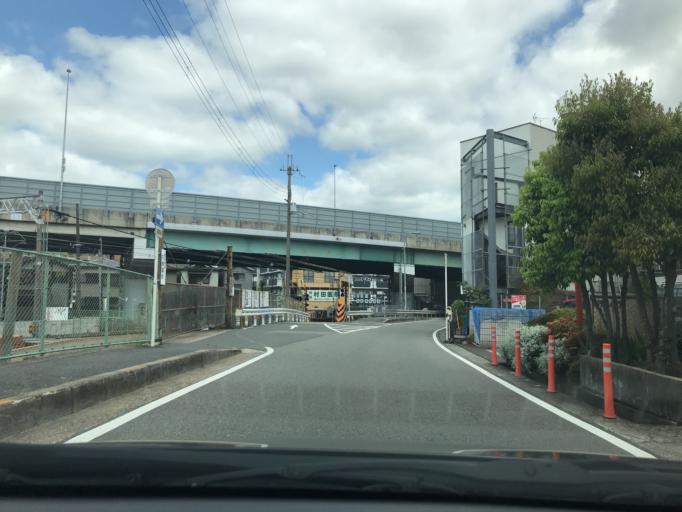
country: JP
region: Osaka
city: Ikeda
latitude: 34.8101
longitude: 135.4489
